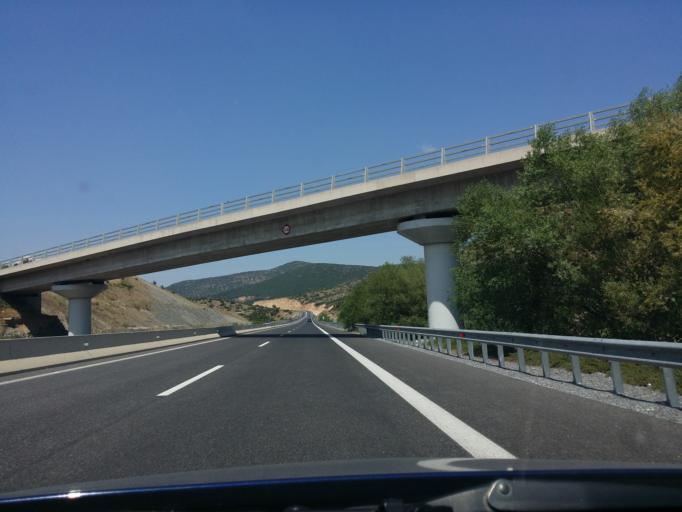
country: GR
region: Peloponnese
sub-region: Nomos Arkadias
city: Megalopoli
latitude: 37.3915
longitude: 22.2885
